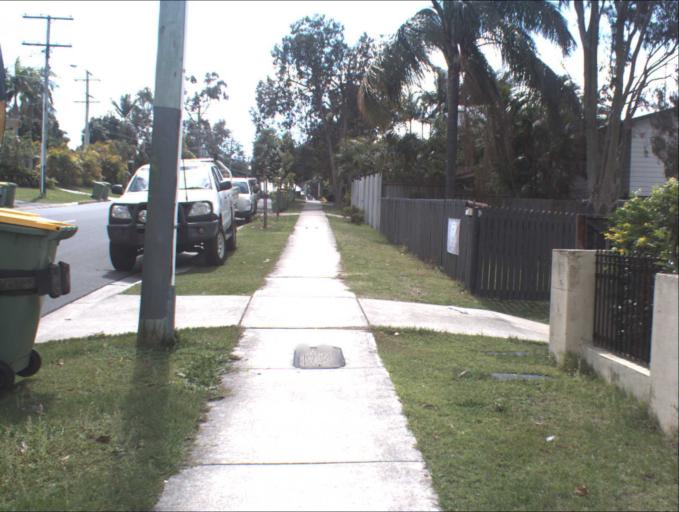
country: AU
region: Queensland
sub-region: Logan
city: Park Ridge South
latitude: -27.6668
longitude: 153.0287
